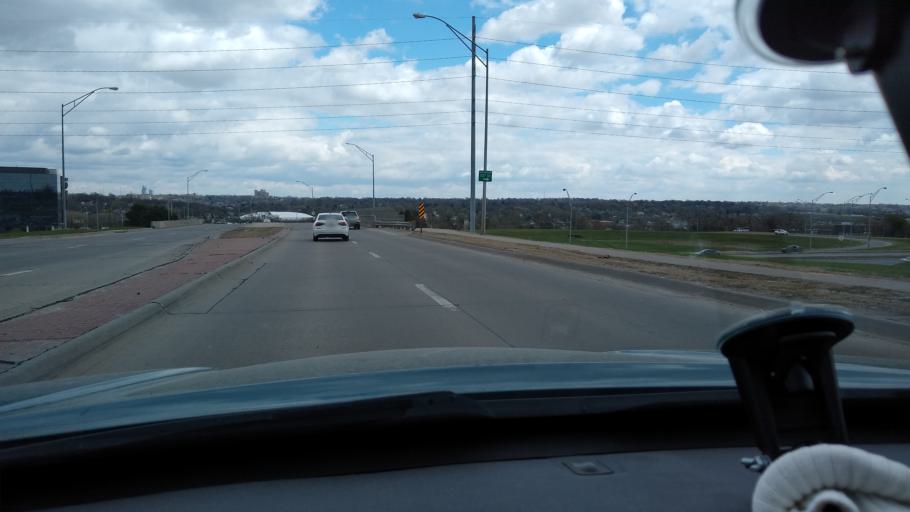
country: US
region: Nebraska
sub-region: Douglas County
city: Ralston
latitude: 41.2343
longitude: -96.0253
